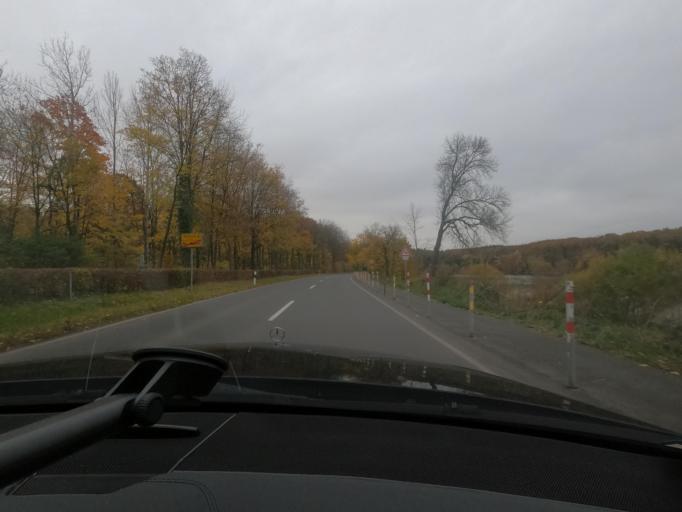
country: DE
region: North Rhine-Westphalia
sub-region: Regierungsbezirk Arnsberg
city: Mohnesee
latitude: 51.4827
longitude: 8.1770
